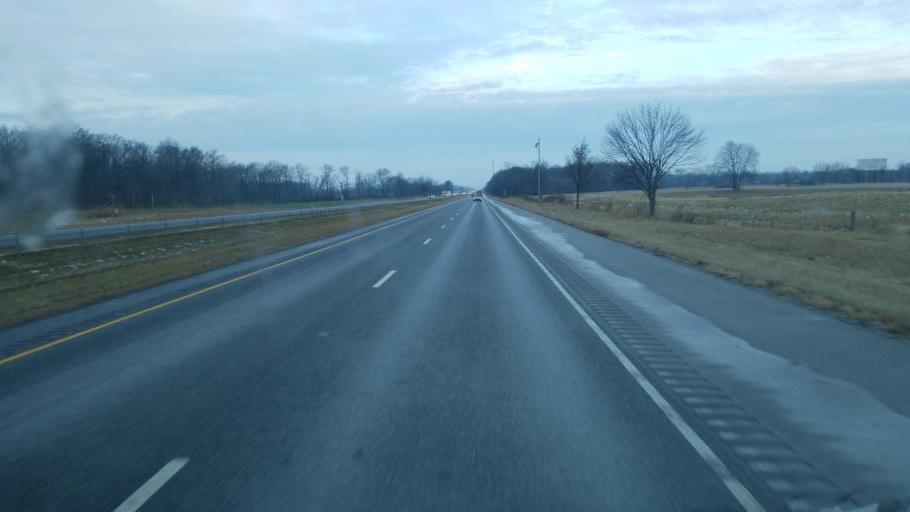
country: US
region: Indiana
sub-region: Hancock County
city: Greenfield
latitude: 39.8206
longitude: -85.8068
